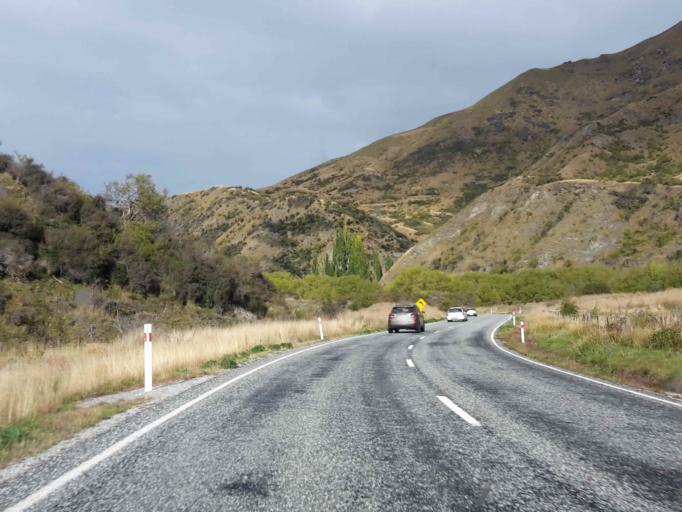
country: NZ
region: Otago
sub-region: Queenstown-Lakes District
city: Arrowtown
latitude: -44.9142
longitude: 168.9752
